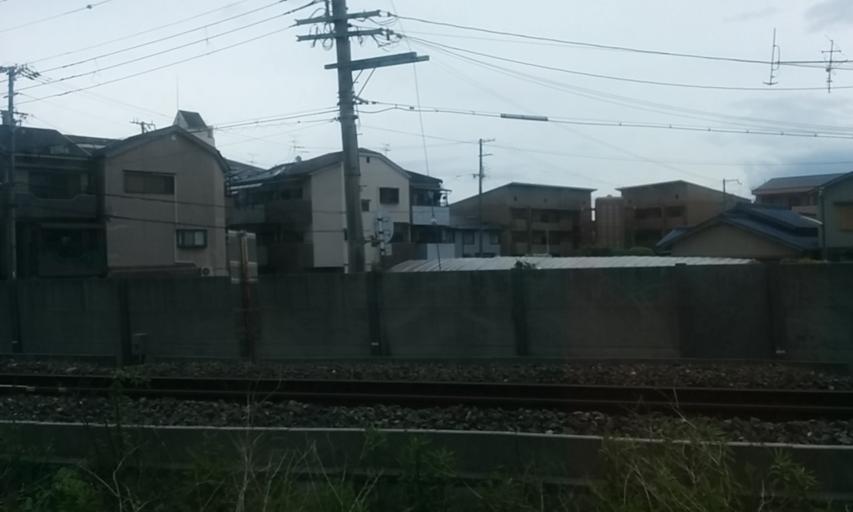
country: JP
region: Osaka
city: Moriguchi
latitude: 34.6871
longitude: 135.5717
